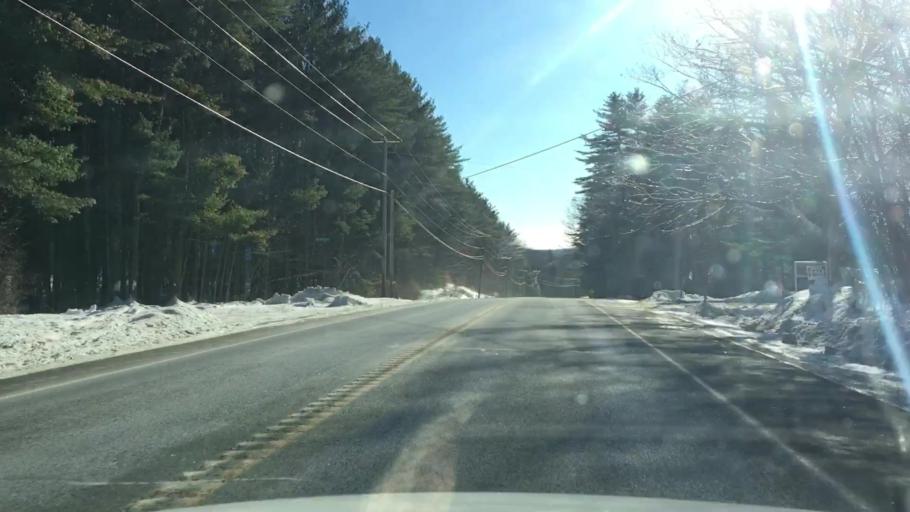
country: US
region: Maine
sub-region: Androscoggin County
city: Greene
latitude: 44.2096
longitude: -70.0988
